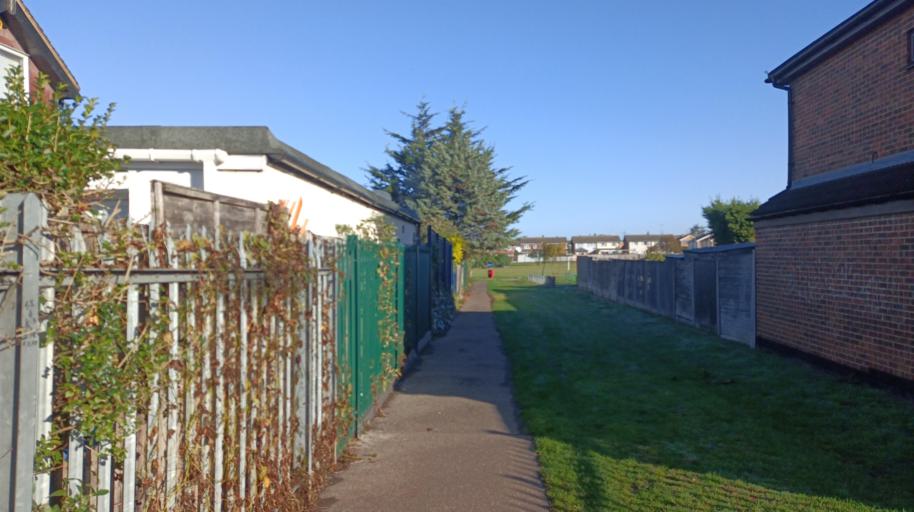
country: GB
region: England
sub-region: Essex
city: South Benfleet
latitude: 51.5695
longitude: 0.5515
